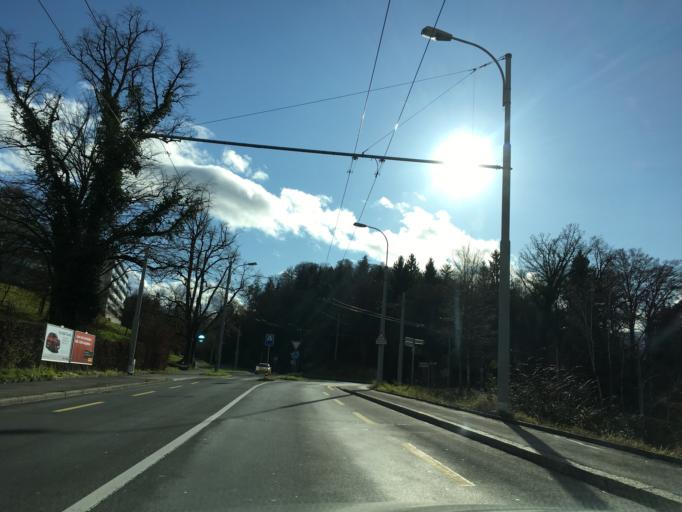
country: CH
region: Lucerne
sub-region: Lucerne-Land District
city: Ebikon
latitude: 47.0664
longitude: 8.3231
